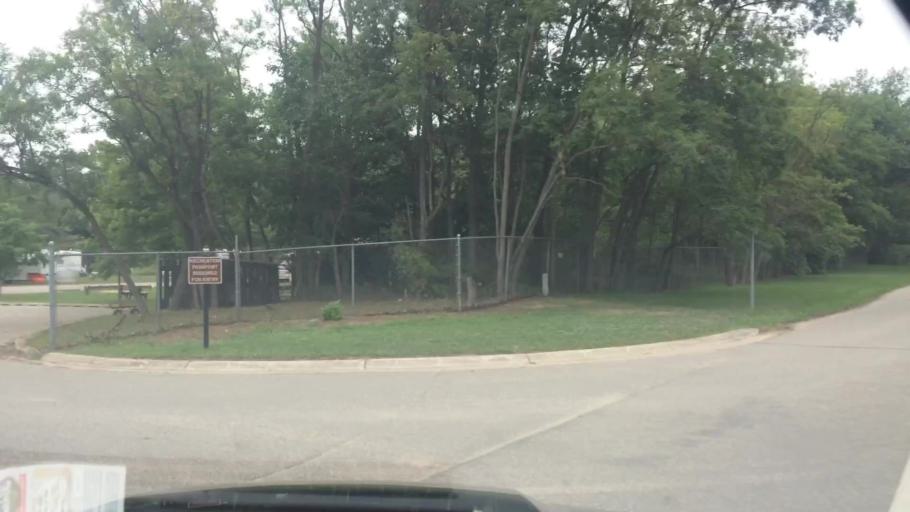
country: US
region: Michigan
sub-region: Huron County
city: Bad Axe
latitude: 44.0069
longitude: -83.0516
